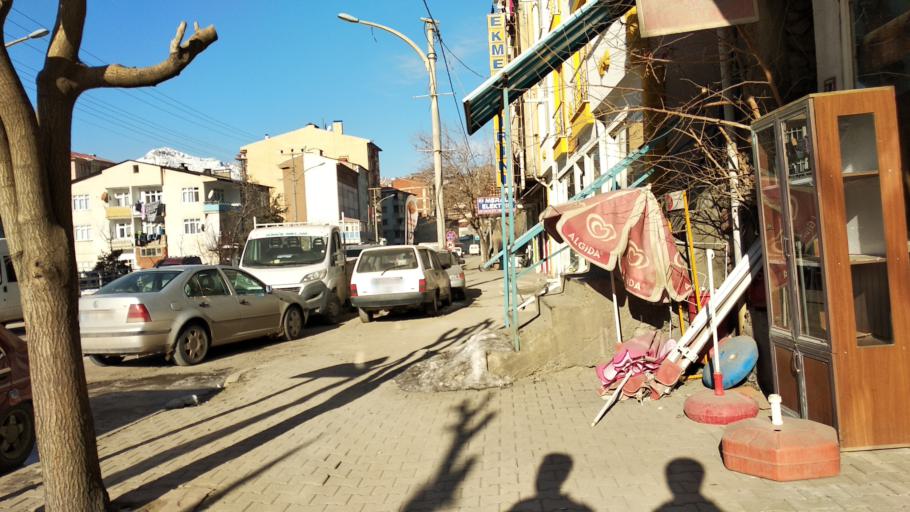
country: TR
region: Gumushane
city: Gumushkhane
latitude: 40.4551
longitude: 39.4915
